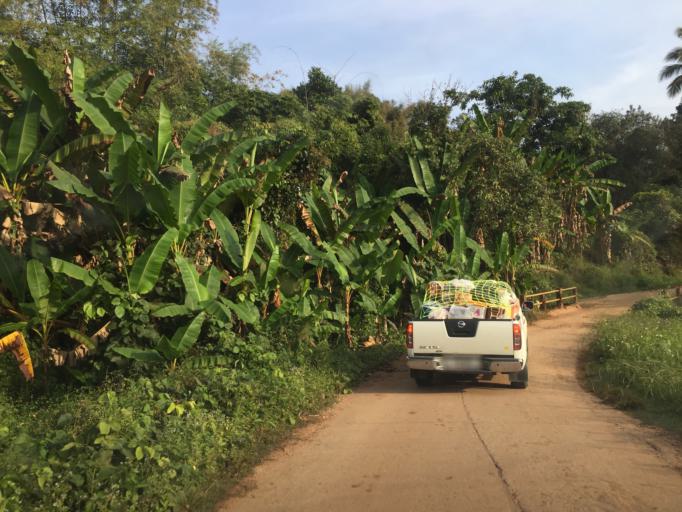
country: TH
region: Chiang Mai
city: Samoeng
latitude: 19.0043
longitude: 98.7065
